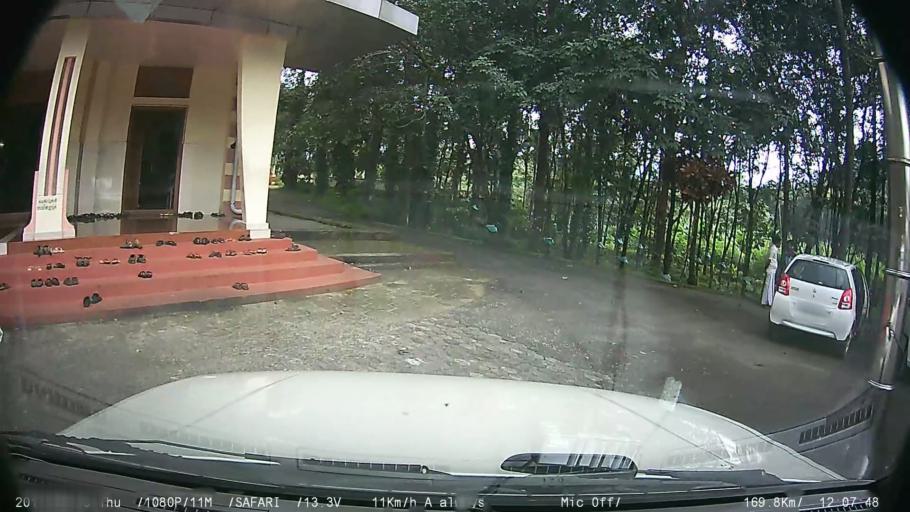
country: IN
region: Kerala
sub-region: Idukki
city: Kuttampuzha
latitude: 10.1051
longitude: 76.6864
